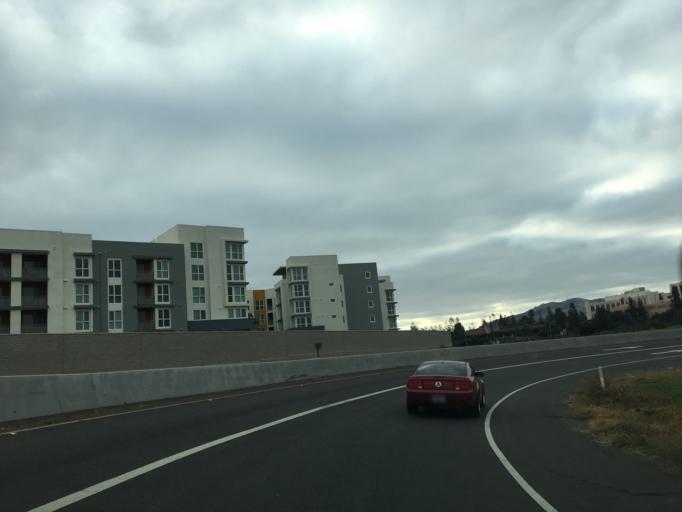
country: US
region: California
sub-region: Santa Clara County
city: Seven Trees
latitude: 37.2440
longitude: -121.8029
